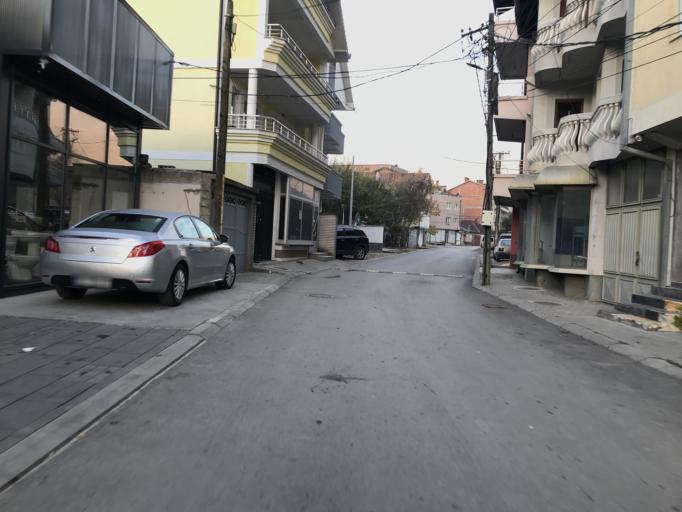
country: XK
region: Pec
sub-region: Komuna e Pejes
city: Peje
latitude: 42.6606
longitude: 20.3007
